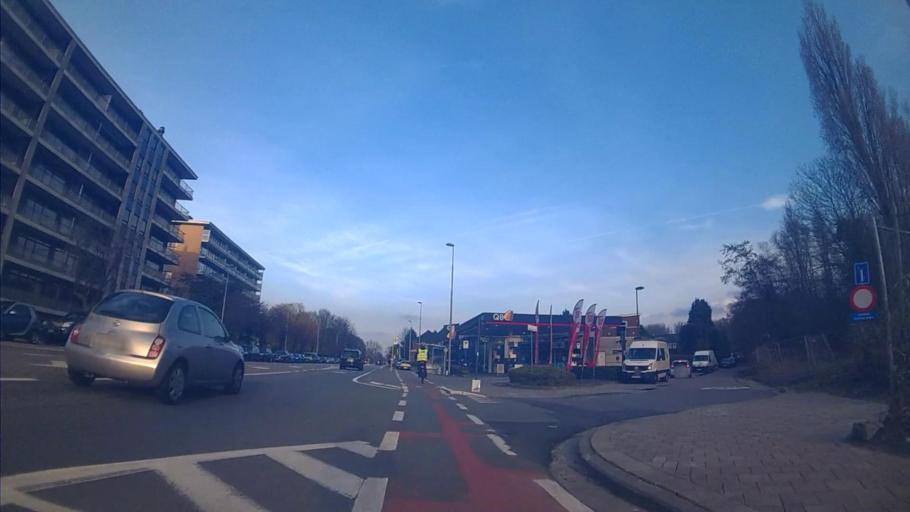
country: BE
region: Flanders
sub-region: Provincie Oost-Vlaanderen
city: Ledeberg
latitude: 51.0605
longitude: 3.7564
